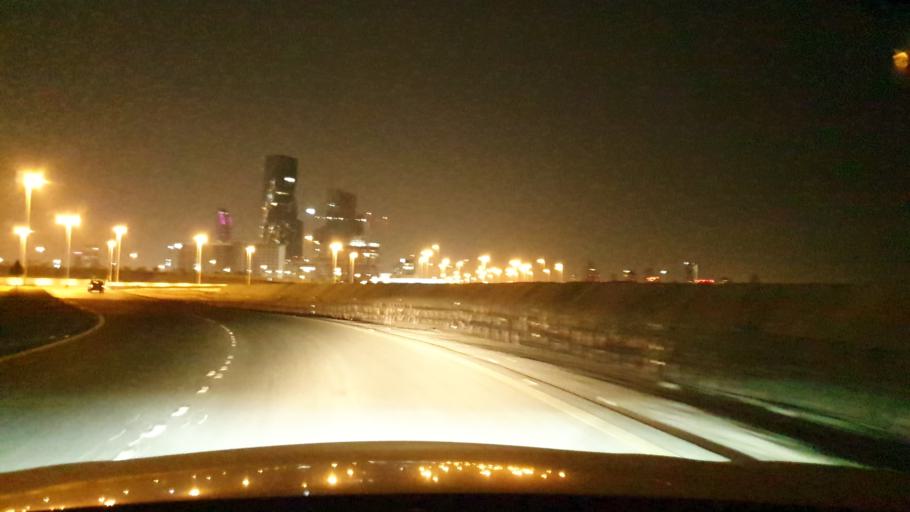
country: BH
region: Muharraq
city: Al Muharraq
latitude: 26.2553
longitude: 50.5815
